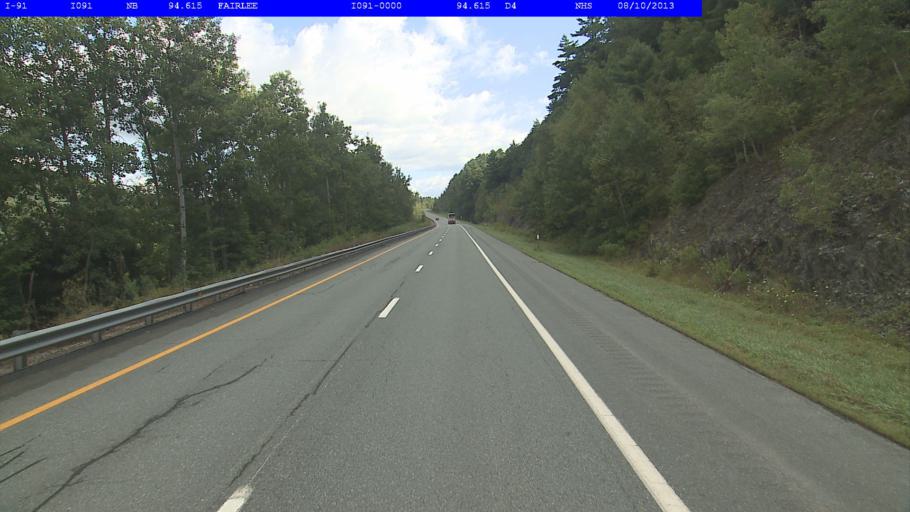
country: US
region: New Hampshire
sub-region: Grafton County
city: Orford
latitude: 43.9418
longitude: -72.1320
